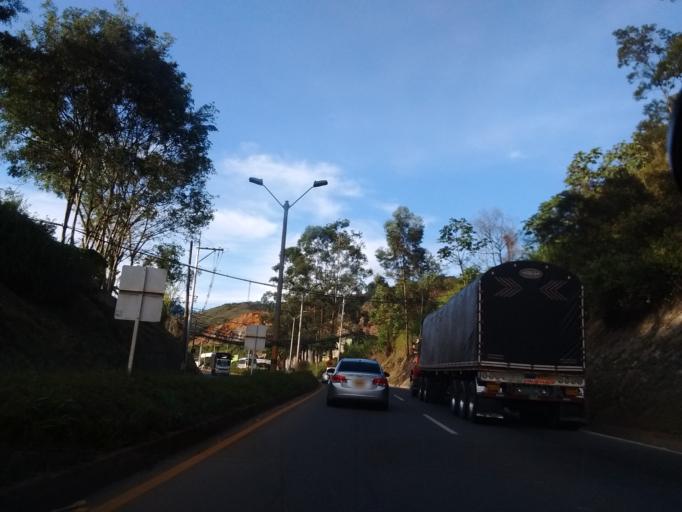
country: CO
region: Antioquia
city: Bello
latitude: 6.3157
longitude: -75.5474
